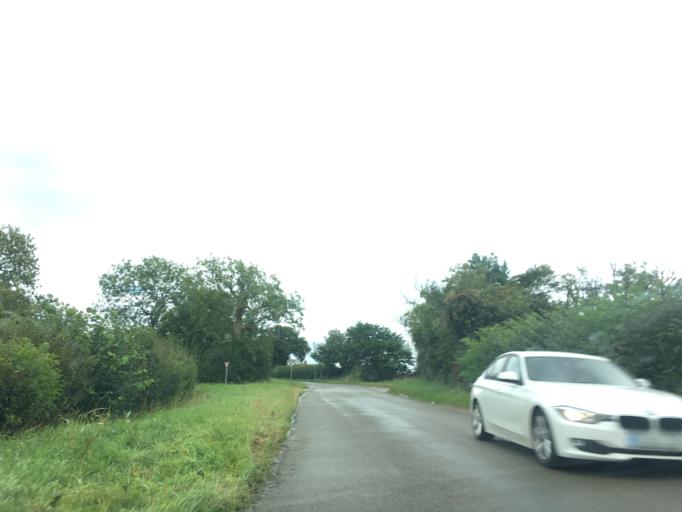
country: GB
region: England
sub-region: Leicestershire
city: Sapcote
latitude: 52.5183
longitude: -1.2759
